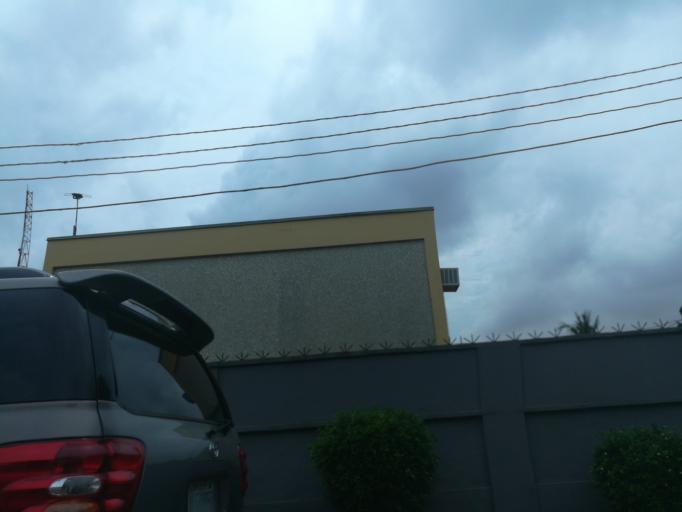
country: NG
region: Lagos
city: Ojota
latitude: 6.5689
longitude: 3.3657
